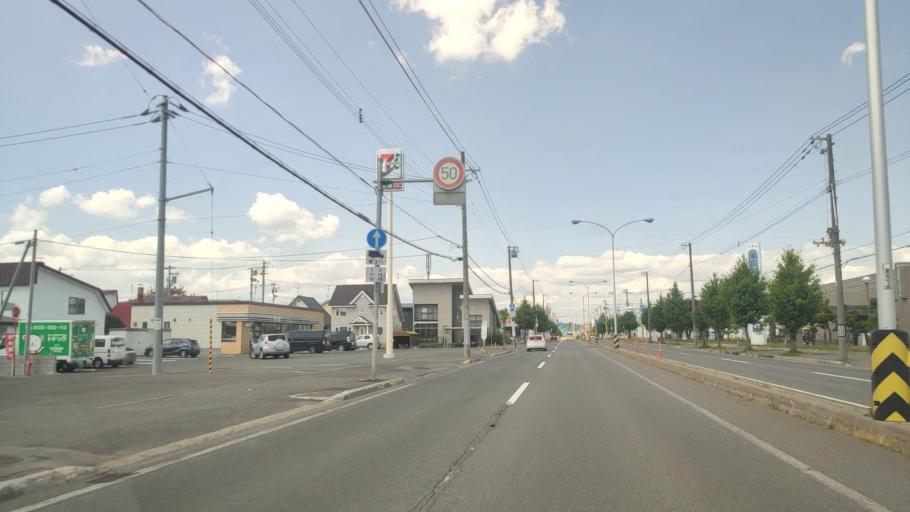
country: JP
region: Hokkaido
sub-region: Asahikawa-shi
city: Asahikawa
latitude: 43.8002
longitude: 142.3931
